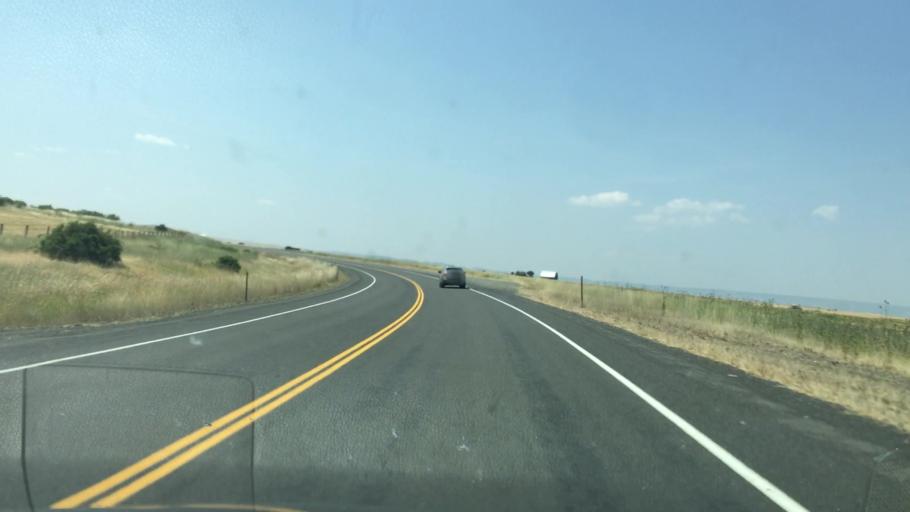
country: US
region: Idaho
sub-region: Idaho County
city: Grangeville
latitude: 45.9246
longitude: -116.1503
